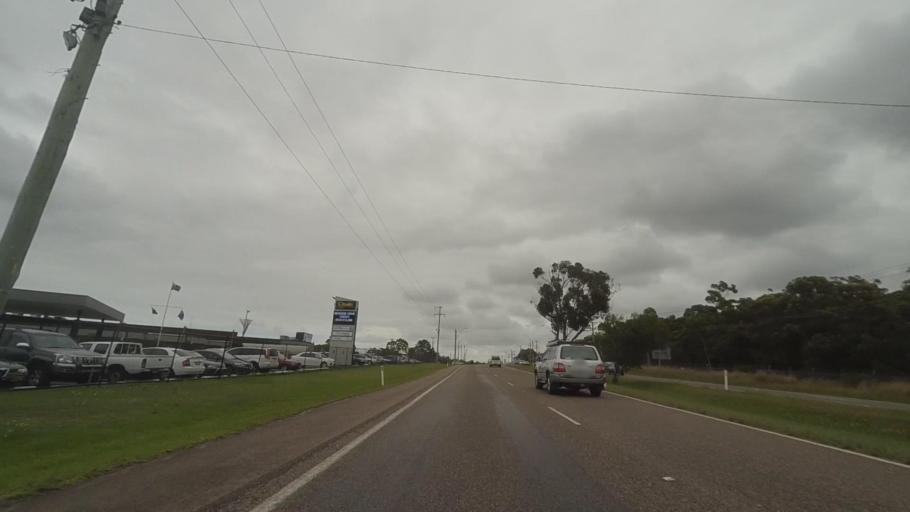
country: AU
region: New South Wales
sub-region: Wyong Shire
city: Buff Point
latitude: -33.1965
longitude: 151.5257
